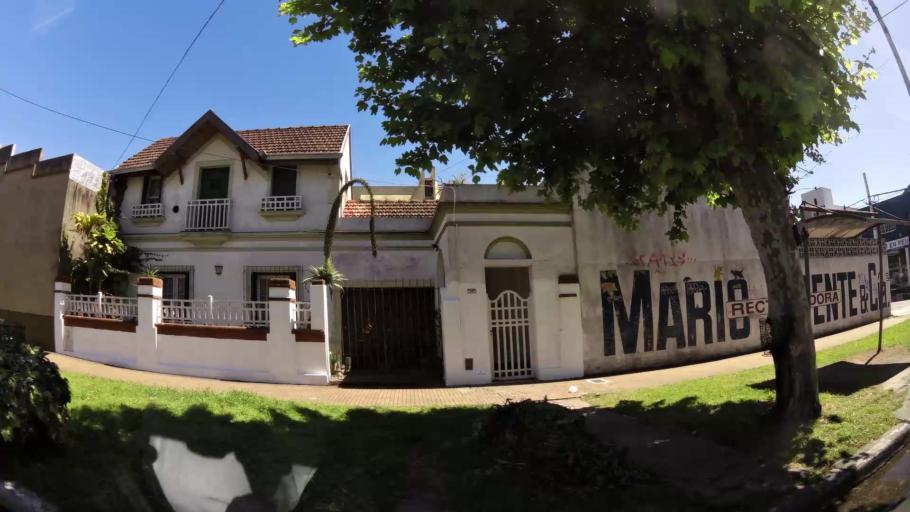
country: AR
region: Buenos Aires
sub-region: Partido de Quilmes
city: Quilmes
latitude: -34.7186
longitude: -58.2697
